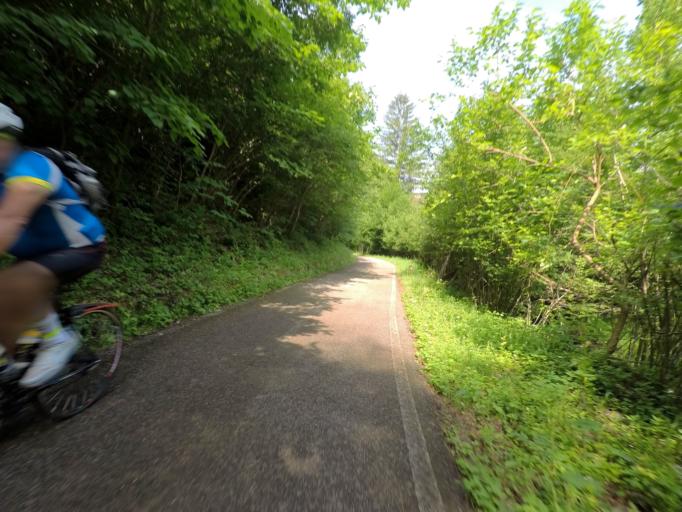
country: IT
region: Friuli Venezia Giulia
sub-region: Provincia di Udine
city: Cavazzo Carnico
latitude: 46.3577
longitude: 13.0670
